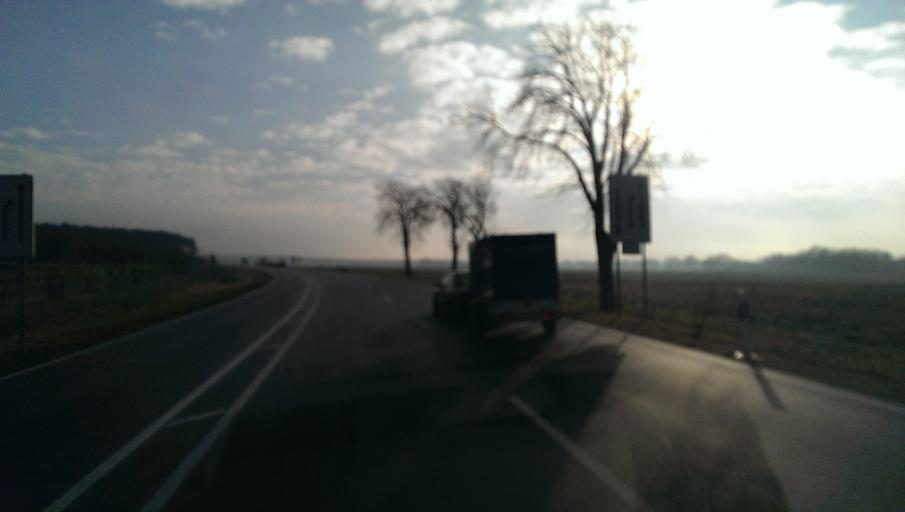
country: DE
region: Brandenburg
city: Herzberg
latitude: 51.6738
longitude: 13.2664
